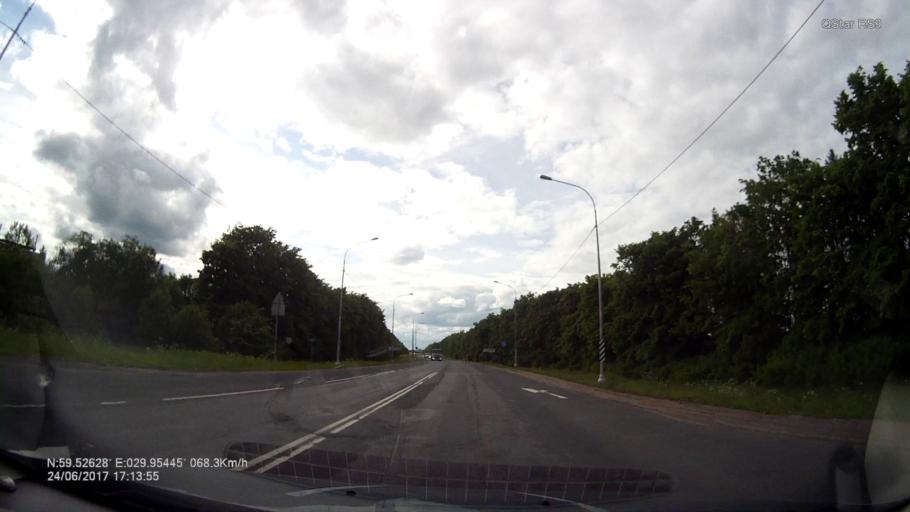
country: RU
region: Leningrad
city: Voyskovitsy
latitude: 59.5266
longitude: 29.9537
